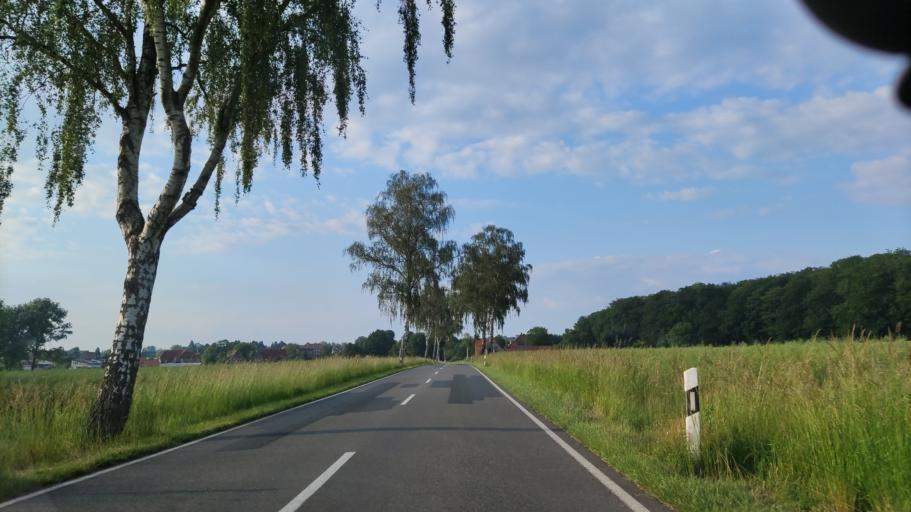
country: DE
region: Lower Saxony
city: Ebstorf
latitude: 53.0126
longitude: 10.4190
